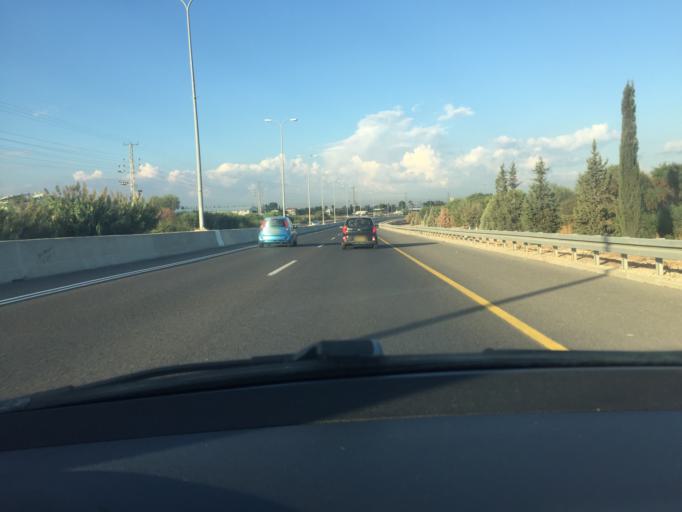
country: IL
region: Central District
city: Lod
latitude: 31.9851
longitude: 34.9232
